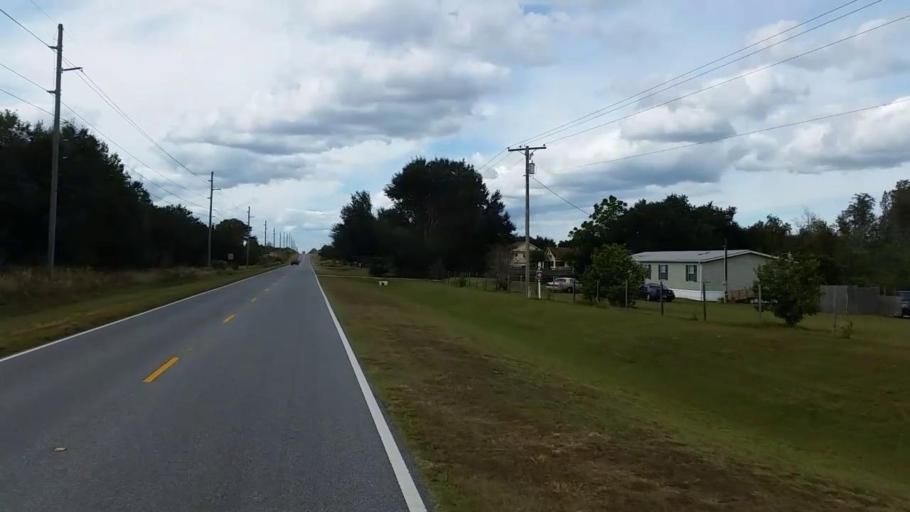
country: US
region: Florida
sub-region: Lake County
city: Four Corners
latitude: 28.3702
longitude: -81.6941
